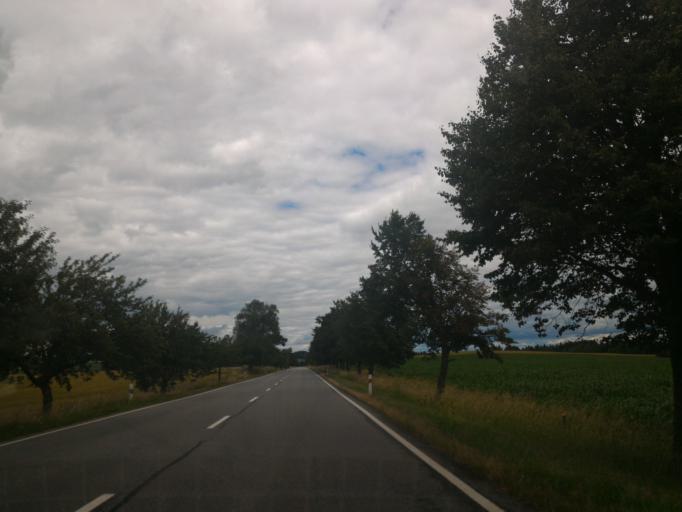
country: CZ
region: Vysocina
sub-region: Okres Pelhrimov
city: Pelhrimov
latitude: 49.4526
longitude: 15.1899
